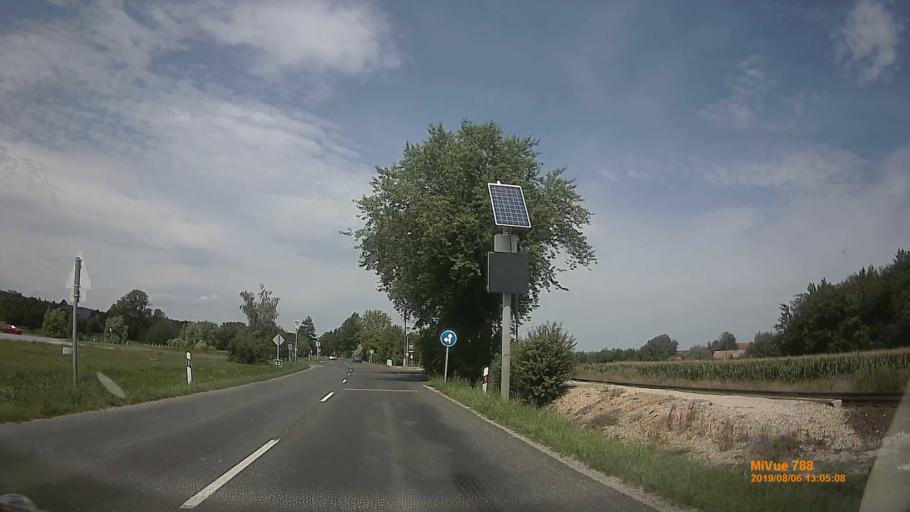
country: HU
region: Vas
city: Koszeg
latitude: 47.3612
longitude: 16.5675
